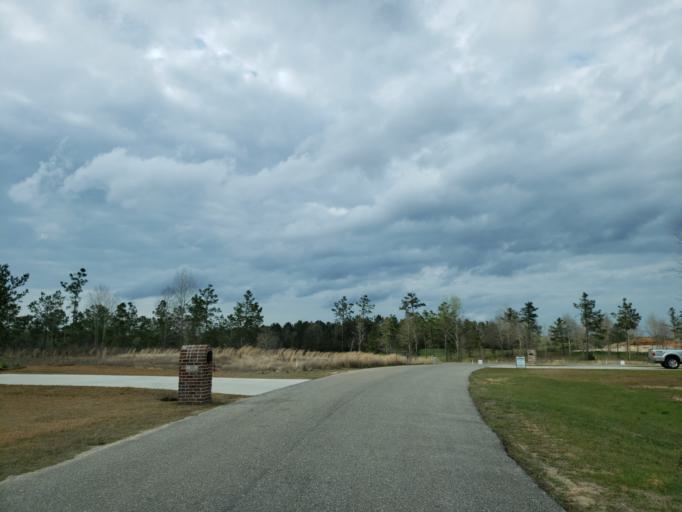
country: US
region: Mississippi
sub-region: Jones County
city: Ellisville
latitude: 31.5558
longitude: -89.2580
